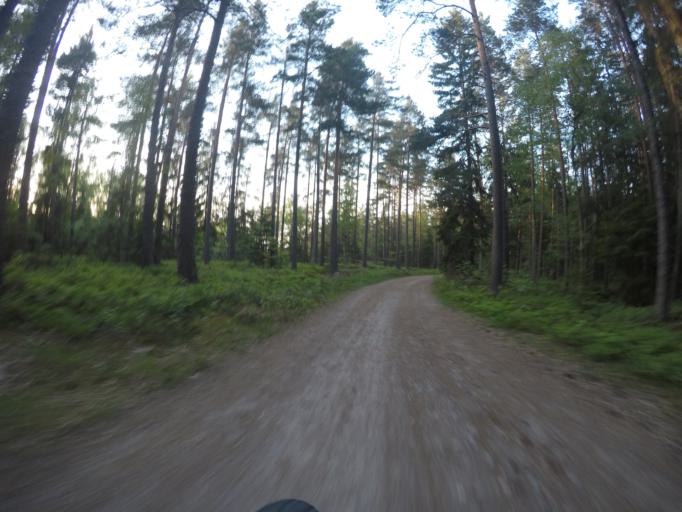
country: SE
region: Soedermanland
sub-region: Eskilstuna Kommun
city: Eskilstuna
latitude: 59.3444
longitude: 16.5108
